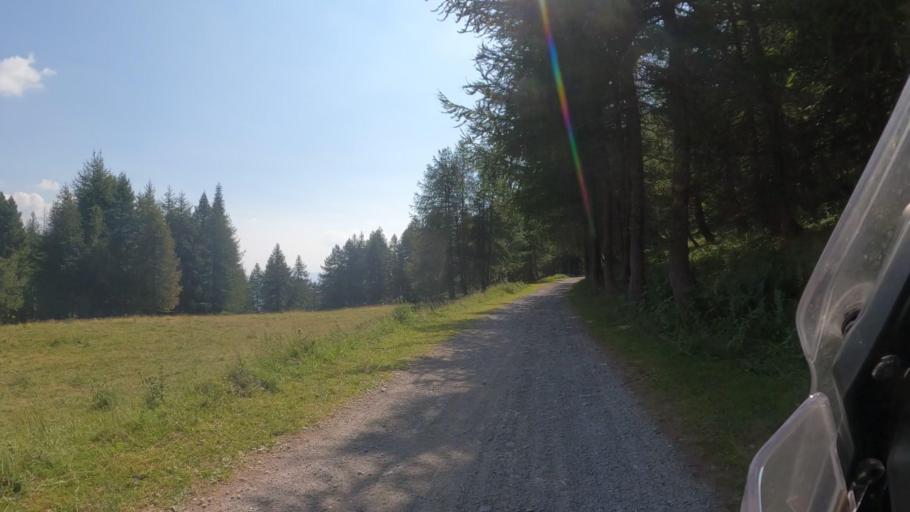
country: IT
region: Piedmont
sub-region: Provincia di Cuneo
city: Briga Alta
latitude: 44.0881
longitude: 7.7258
